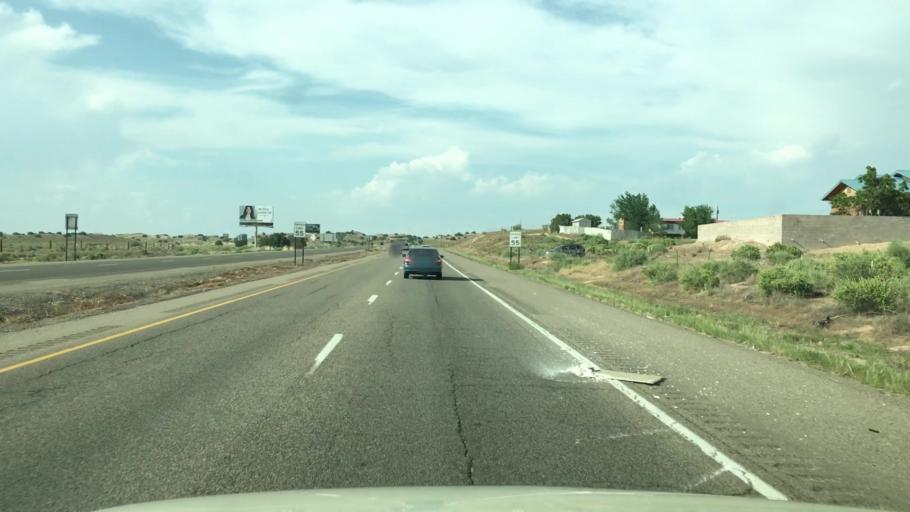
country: US
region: New Mexico
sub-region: Santa Fe County
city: Pojoaque
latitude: 35.9103
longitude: -106.0174
